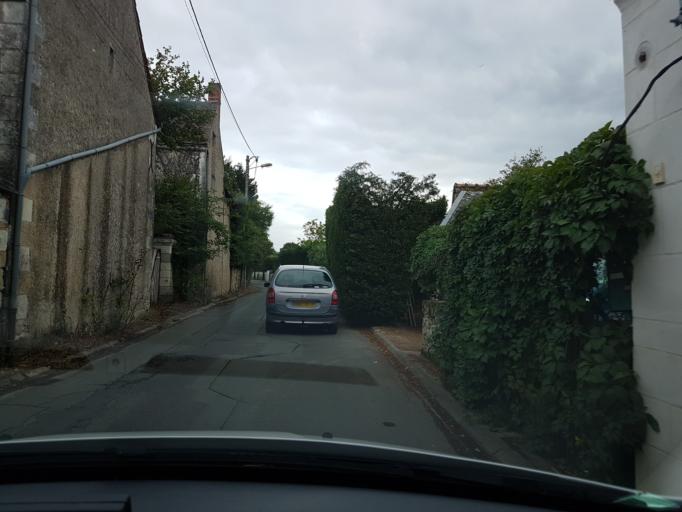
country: FR
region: Centre
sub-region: Departement d'Indre-et-Loire
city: Saint-Avertin
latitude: 47.3621
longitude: 0.7584
